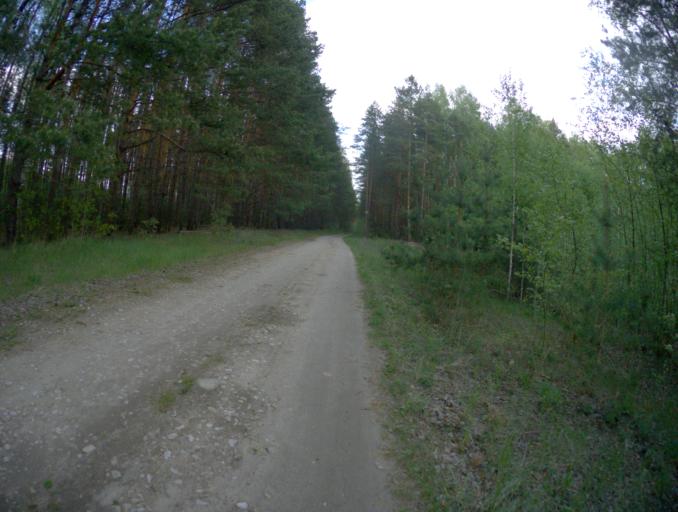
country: RU
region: Rjazan
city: Spas-Klepiki
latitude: 55.2387
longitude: 40.0581
